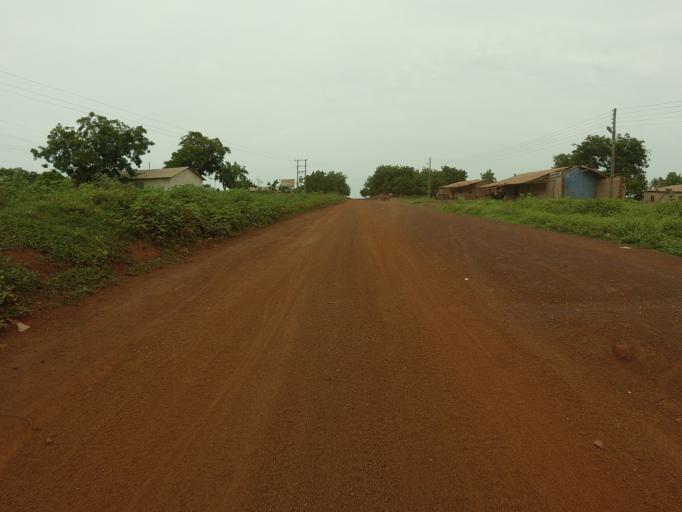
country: GH
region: Northern
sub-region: Yendi
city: Yendi
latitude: 9.0364
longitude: -0.0130
